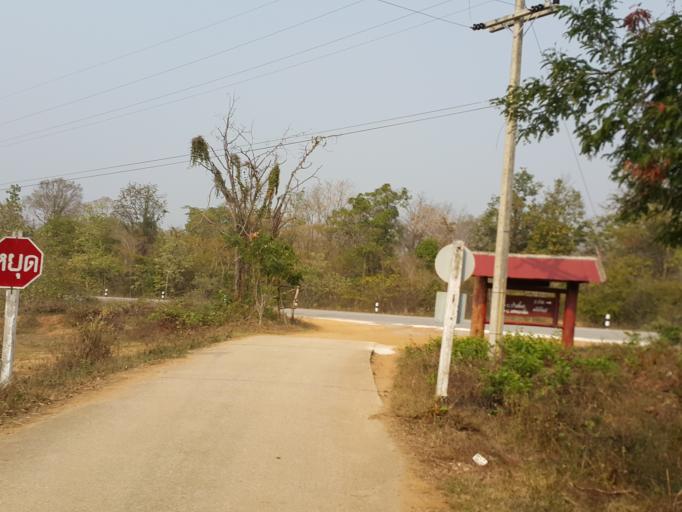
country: TH
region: Lampang
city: Mae Phrik
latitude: 17.4905
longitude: 99.0888
